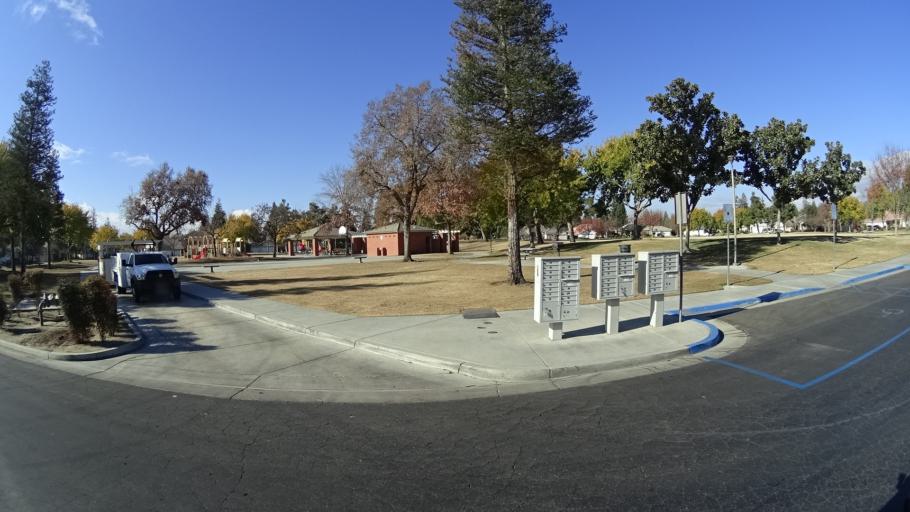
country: US
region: California
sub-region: Kern County
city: Greenacres
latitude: 35.3438
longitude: -119.1210
